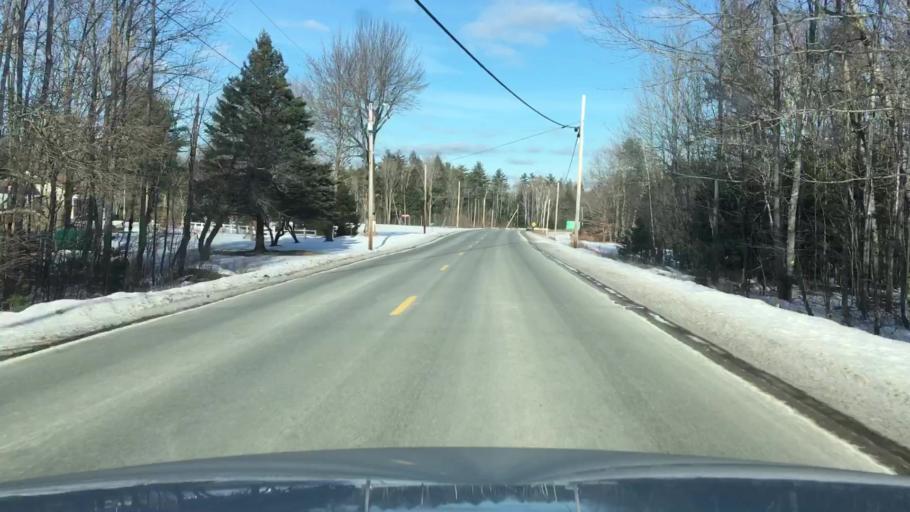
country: US
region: Maine
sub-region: Penobscot County
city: Holden
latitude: 44.7488
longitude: -68.6127
